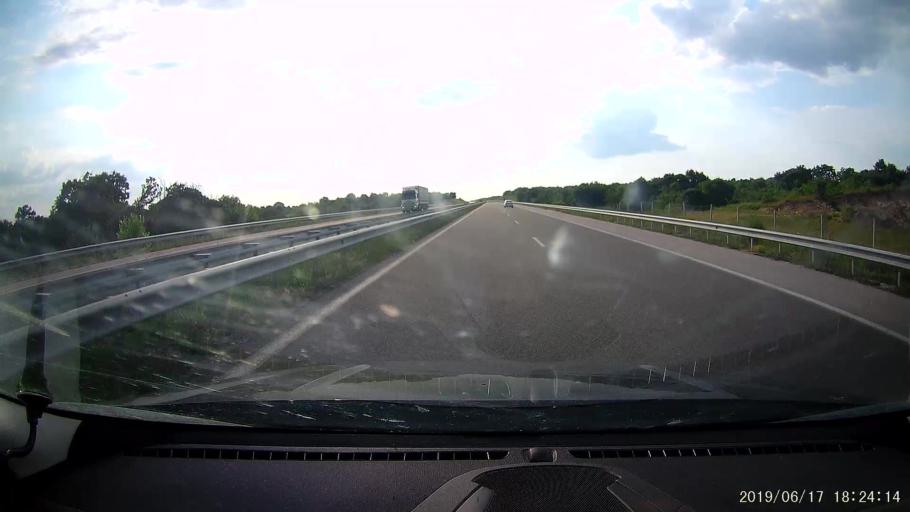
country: BG
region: Khaskovo
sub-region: Obshtina Dimitrovgrad
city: Dimitrovgrad
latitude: 41.9822
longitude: 25.6976
